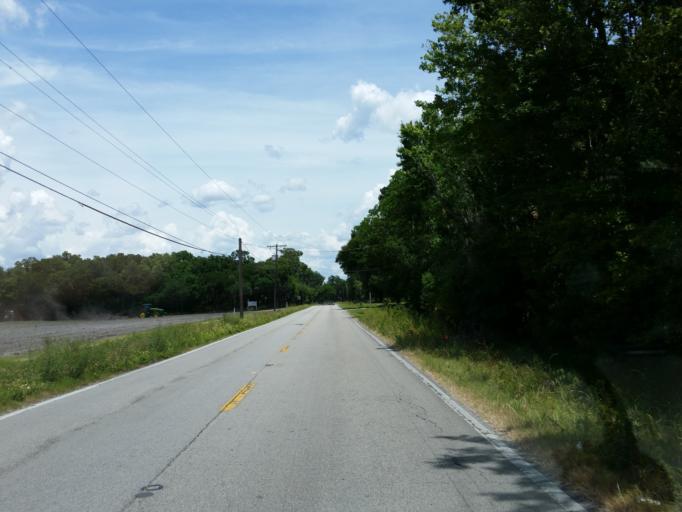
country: US
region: Florida
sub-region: Hillsborough County
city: Dover
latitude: 28.0470
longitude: -82.1976
